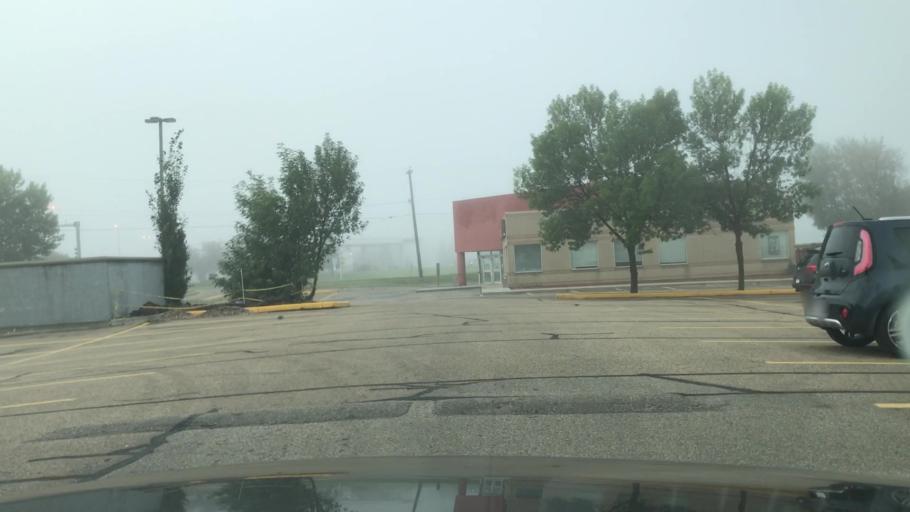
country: CA
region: Alberta
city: Edmonton
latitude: 53.5407
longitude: -113.4272
